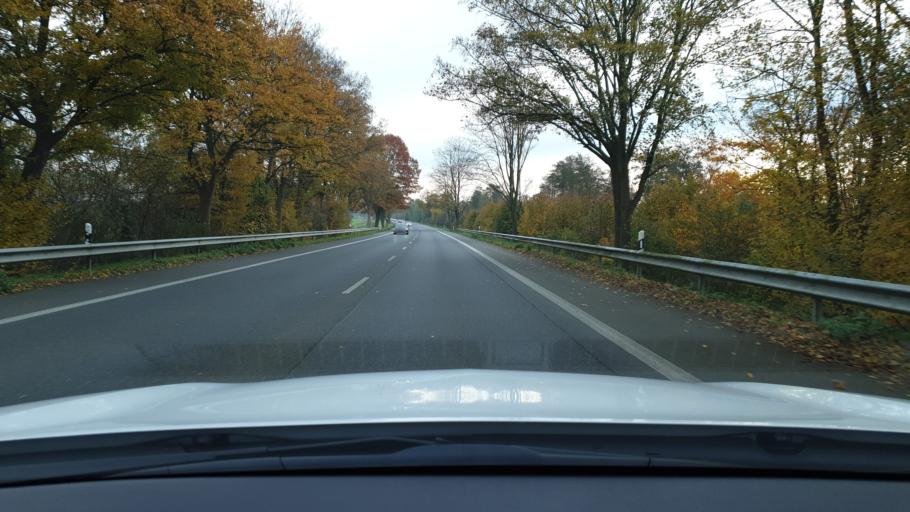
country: NL
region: Gelderland
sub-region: Gemeente Groesbeek
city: De Horst
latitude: 51.8040
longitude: 5.9821
